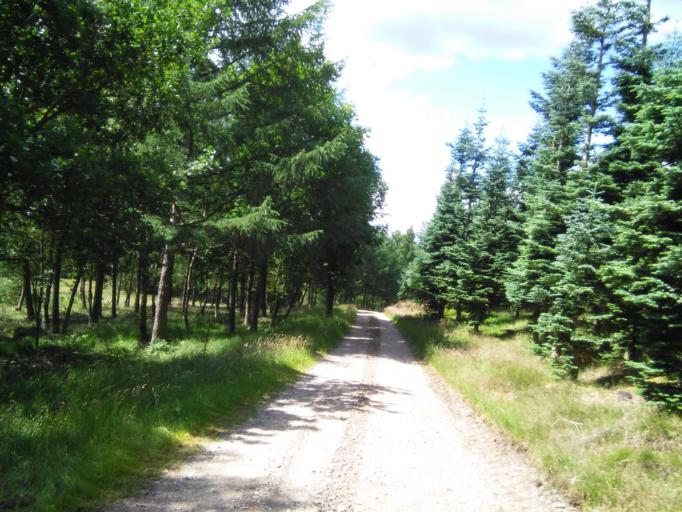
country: DK
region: Central Jutland
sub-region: Silkeborg Kommune
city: Virklund
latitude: 56.0645
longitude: 9.4589
